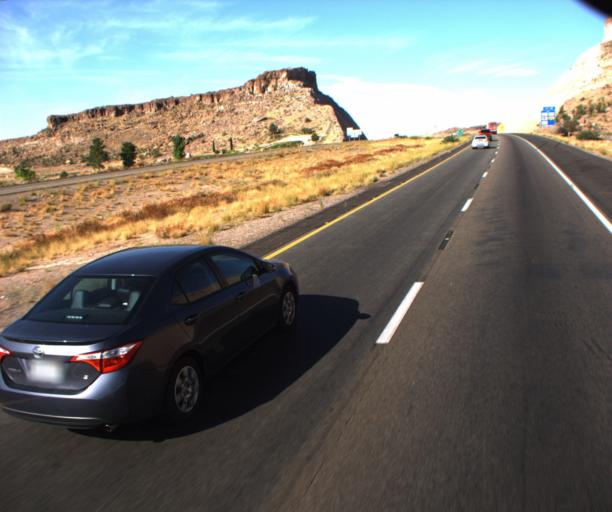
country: US
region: Arizona
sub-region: Mohave County
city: Kingman
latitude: 35.2118
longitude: -114.0545
